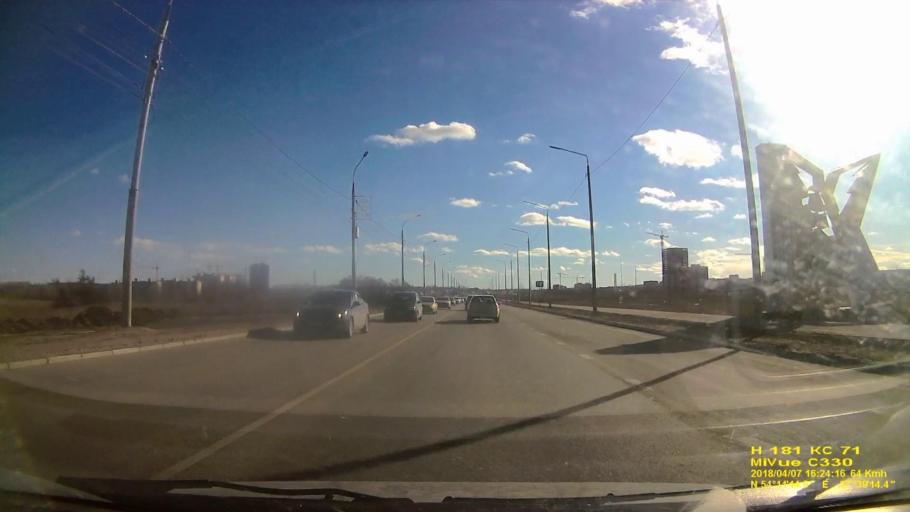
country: RU
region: Tula
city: Tula
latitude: 54.1877
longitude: 37.6478
